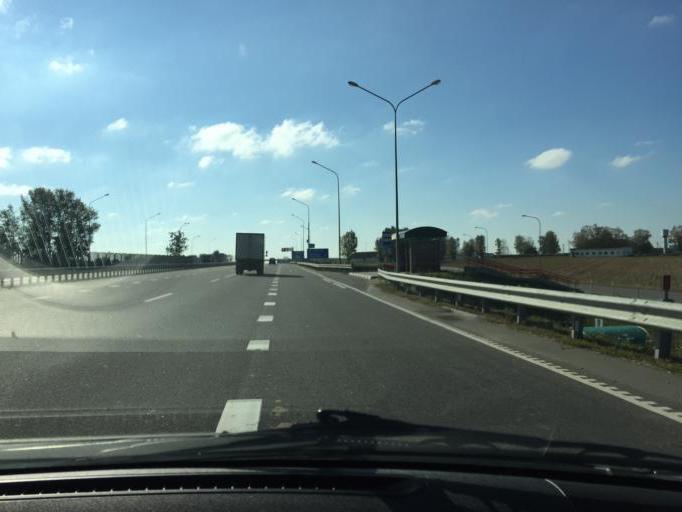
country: BY
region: Minsk
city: Slutsk
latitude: 53.0748
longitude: 27.5596
